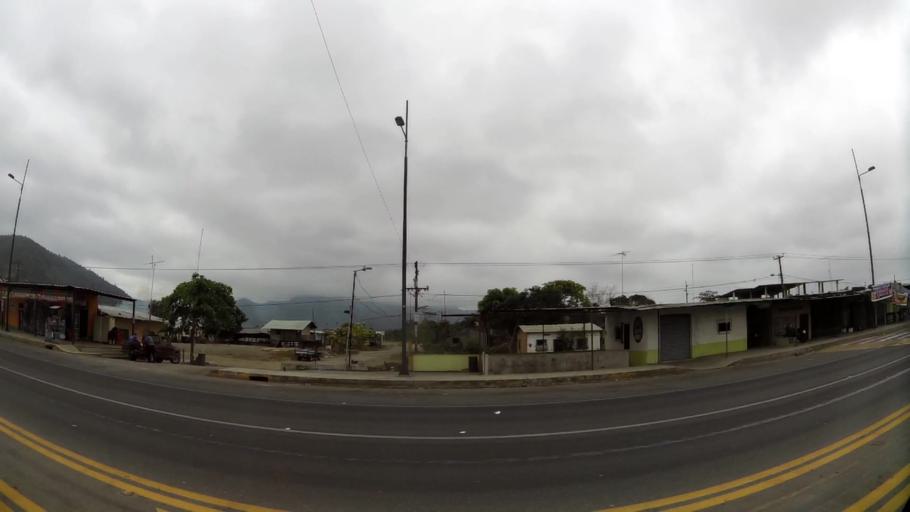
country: EC
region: Guayas
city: Naranjal
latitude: -2.4720
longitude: -79.6212
